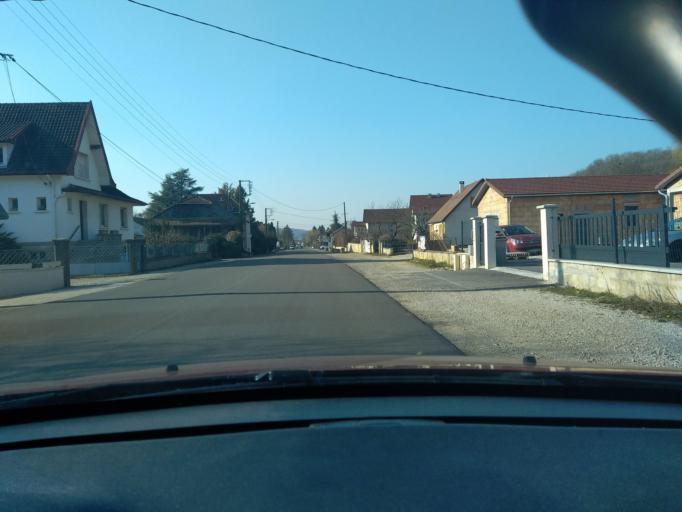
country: FR
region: Franche-Comte
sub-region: Departement du Jura
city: Perrigny
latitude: 46.6604
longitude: 5.5898
